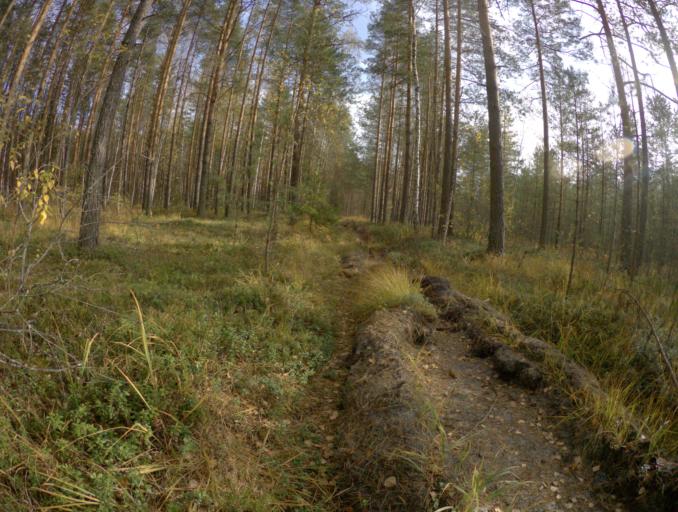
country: RU
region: Vladimir
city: Raduzhnyy
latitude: 55.9387
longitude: 40.3284
